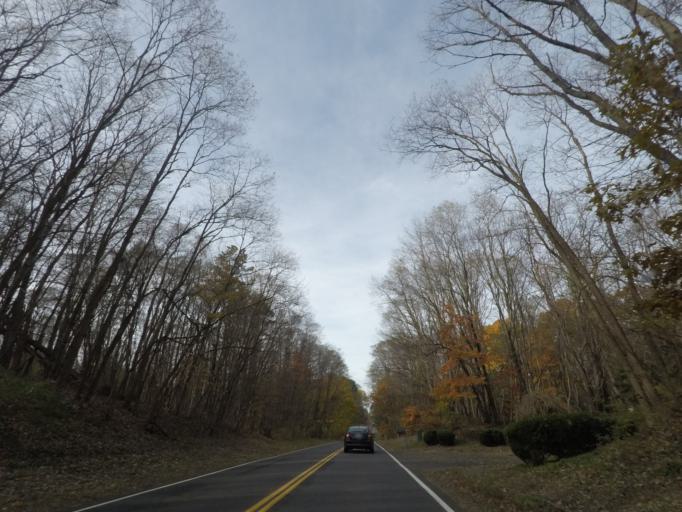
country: US
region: New York
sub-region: Albany County
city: Westmere
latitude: 42.7284
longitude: -73.8985
